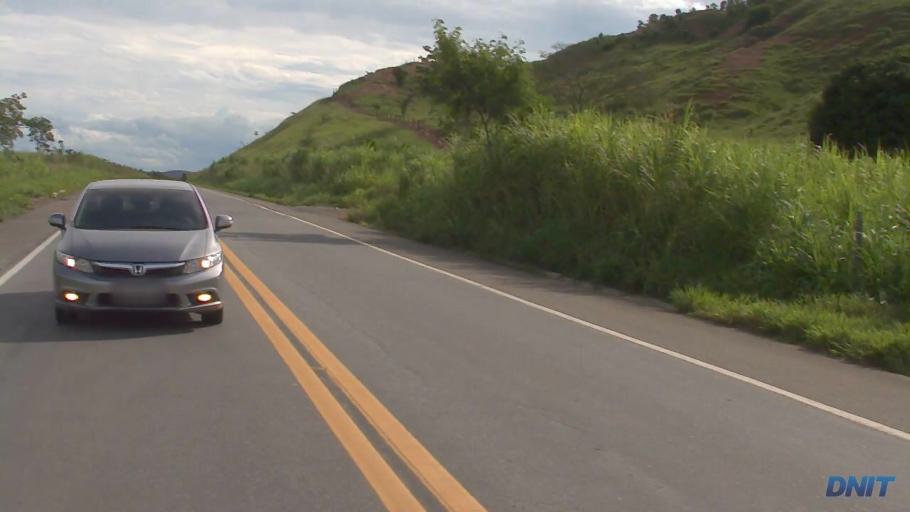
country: BR
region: Minas Gerais
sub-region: Belo Oriente
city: Belo Oriente
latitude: -19.1847
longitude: -42.2643
